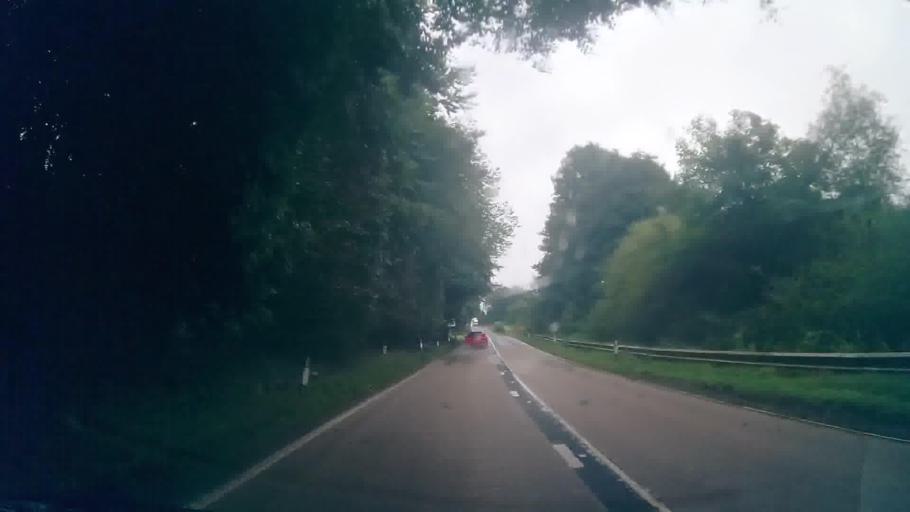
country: GB
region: Scotland
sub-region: Dumfries and Galloway
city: Dumfries
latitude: 55.1446
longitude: -3.6949
